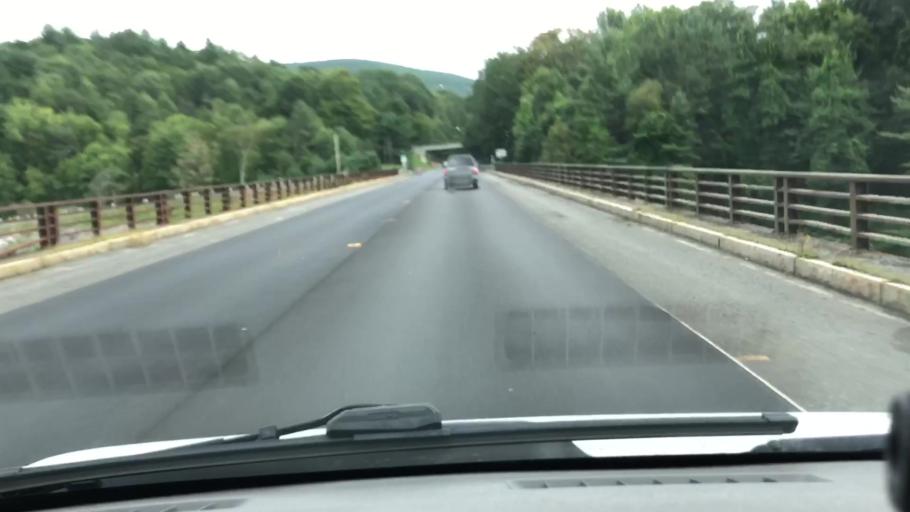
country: US
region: Massachusetts
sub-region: Franklin County
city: Shelburne Falls
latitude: 42.6188
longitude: -72.7475
